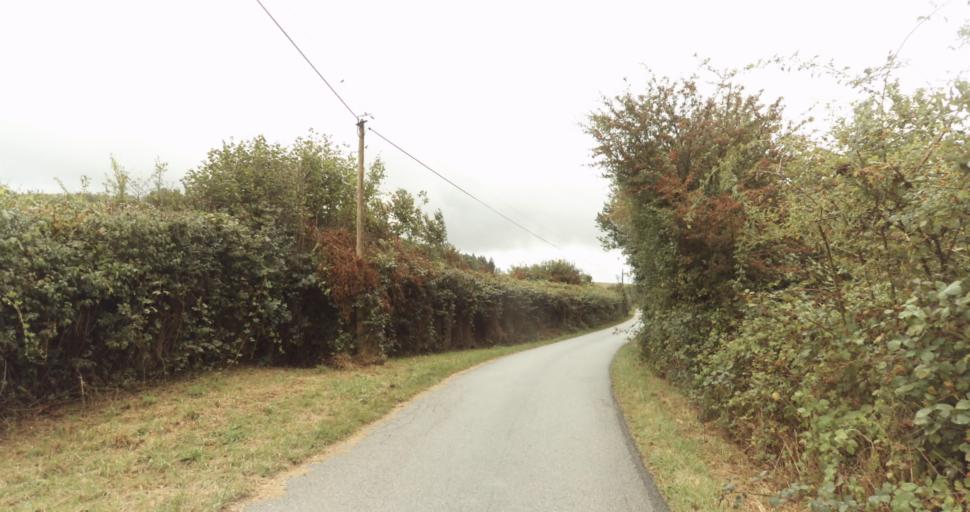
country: FR
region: Lower Normandy
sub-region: Departement de l'Orne
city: Sainte-Gauburge-Sainte-Colombe
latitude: 48.7014
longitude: 0.4310
